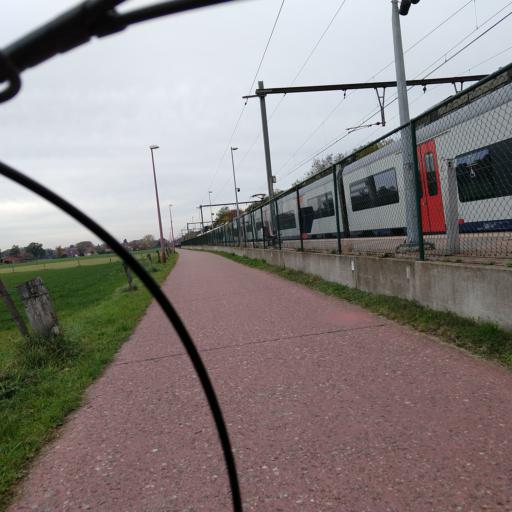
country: BE
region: Flanders
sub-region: Provincie Antwerpen
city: Kalmthout
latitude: 51.3791
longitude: 4.4672
